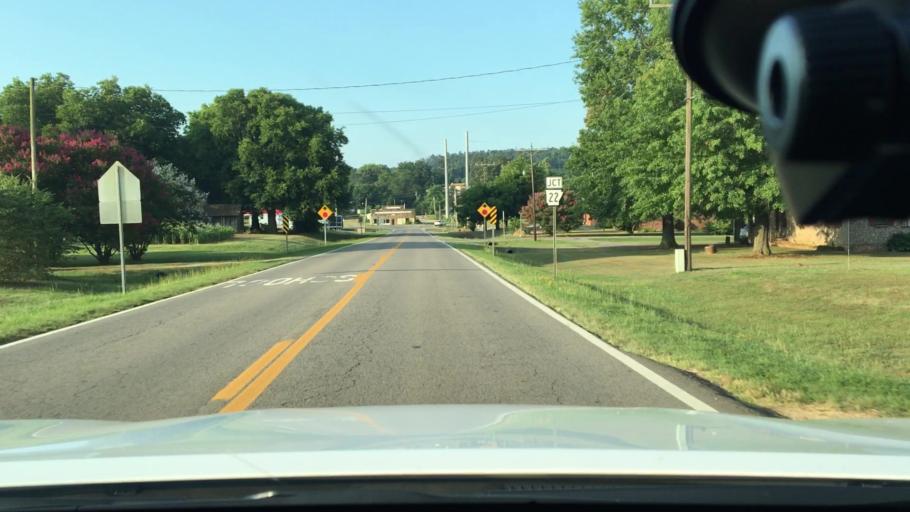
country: US
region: Arkansas
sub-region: Logan County
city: Paris
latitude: 35.2960
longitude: -93.6365
